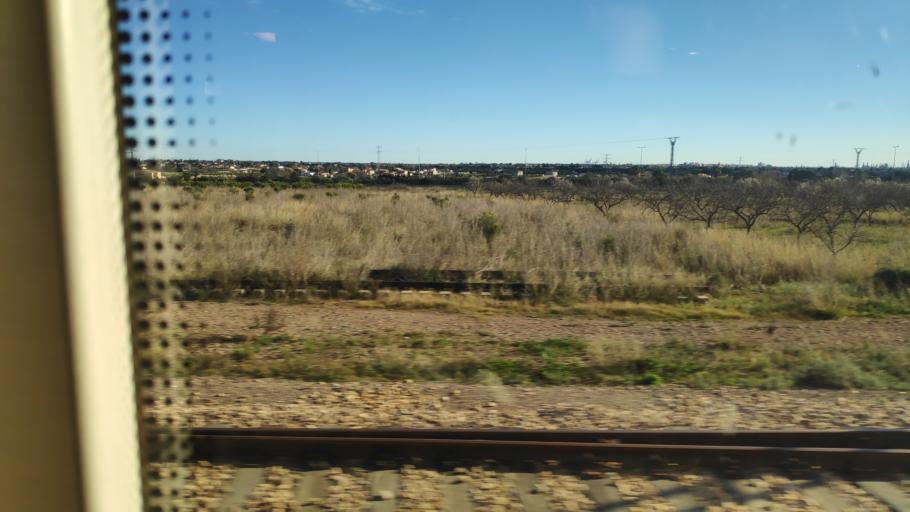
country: ES
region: Valencia
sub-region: Provincia de Castello
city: Castello de la Plana
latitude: 40.0256
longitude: 0.0038
